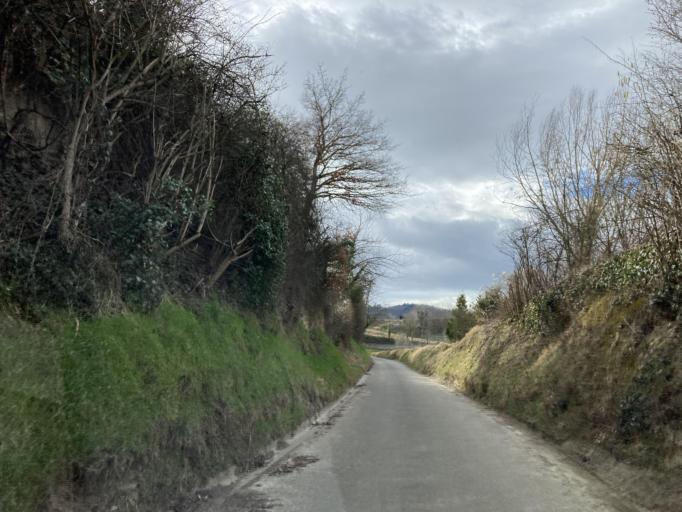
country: DE
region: Baden-Wuerttemberg
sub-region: Freiburg Region
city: Endingen
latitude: 48.1342
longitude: 7.7030
